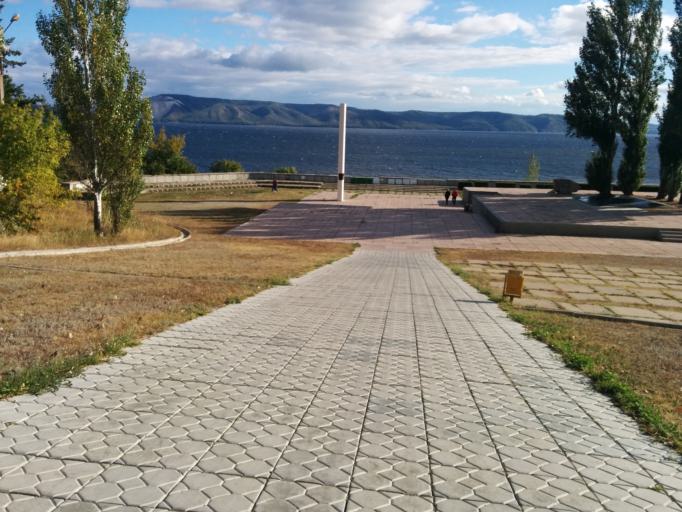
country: RU
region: Samara
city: Tol'yatti
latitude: 53.4745
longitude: 49.3492
